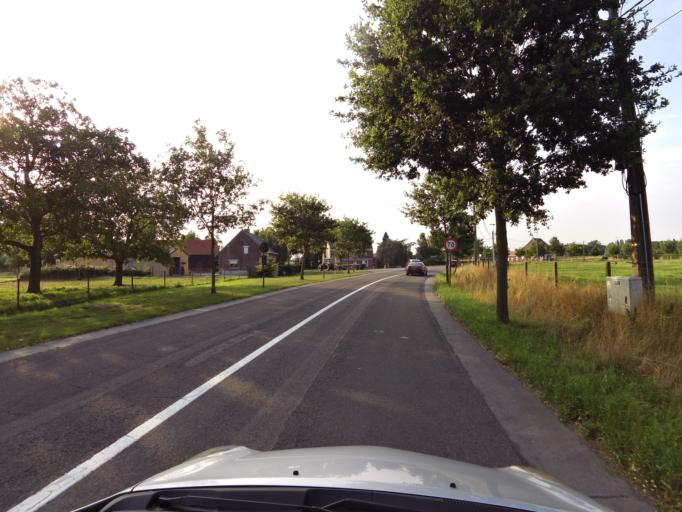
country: BE
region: Flanders
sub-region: Provincie West-Vlaanderen
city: Torhout
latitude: 51.1105
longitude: 3.0806
